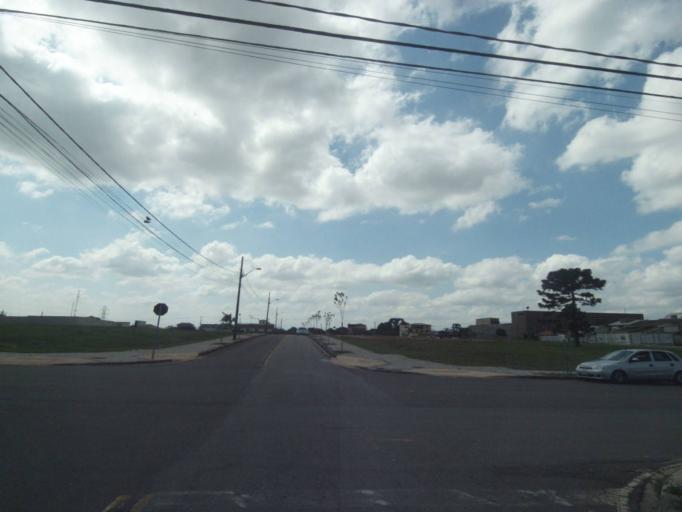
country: BR
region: Parana
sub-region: Curitiba
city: Curitiba
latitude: -25.5043
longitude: -49.3132
